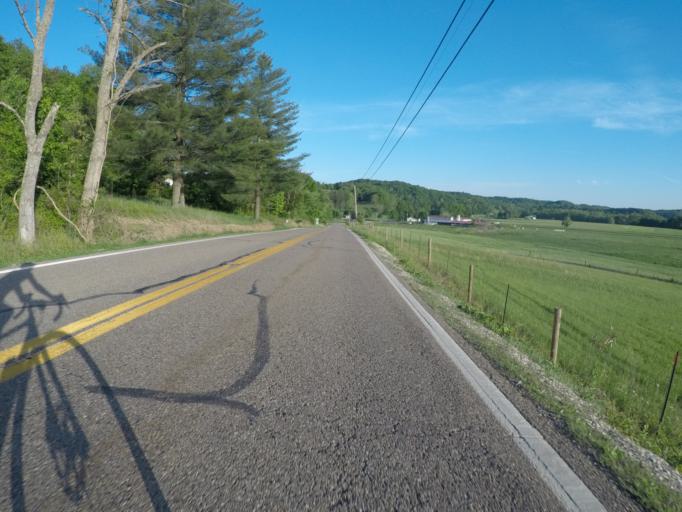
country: US
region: West Virginia
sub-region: Cabell County
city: Huntington
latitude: 38.5448
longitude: -82.4634
